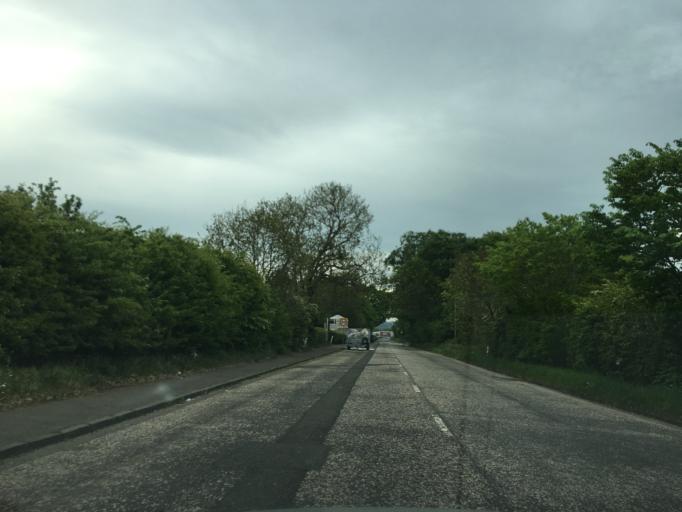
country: GB
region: Scotland
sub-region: Edinburgh
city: Currie
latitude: 55.9437
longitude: -3.3211
